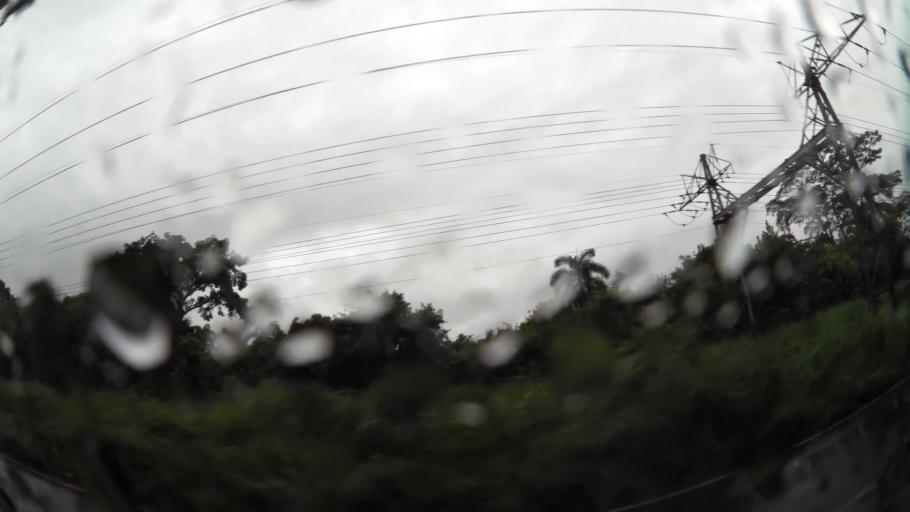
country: PA
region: Panama
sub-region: Distrito de Panama
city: Paraiso
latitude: 9.0154
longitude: -79.6049
